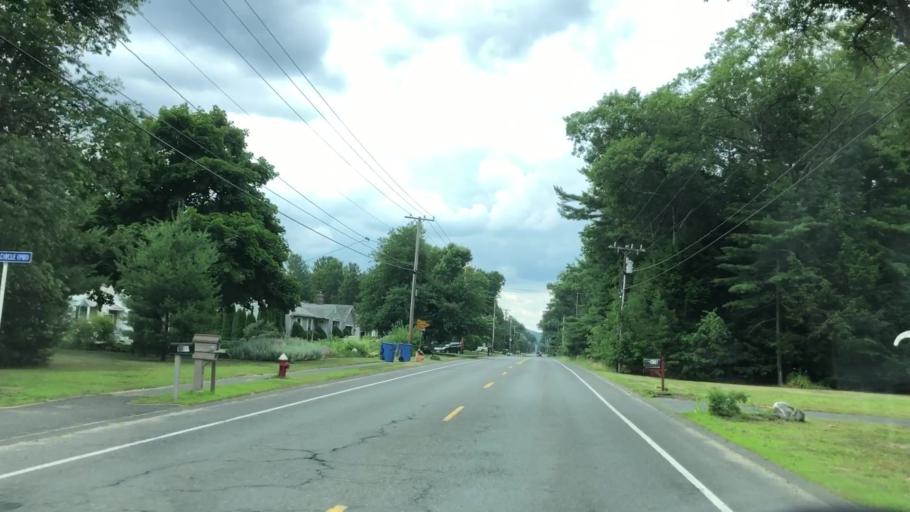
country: US
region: Massachusetts
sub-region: Hampshire County
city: Southampton
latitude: 42.2075
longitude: -72.6896
